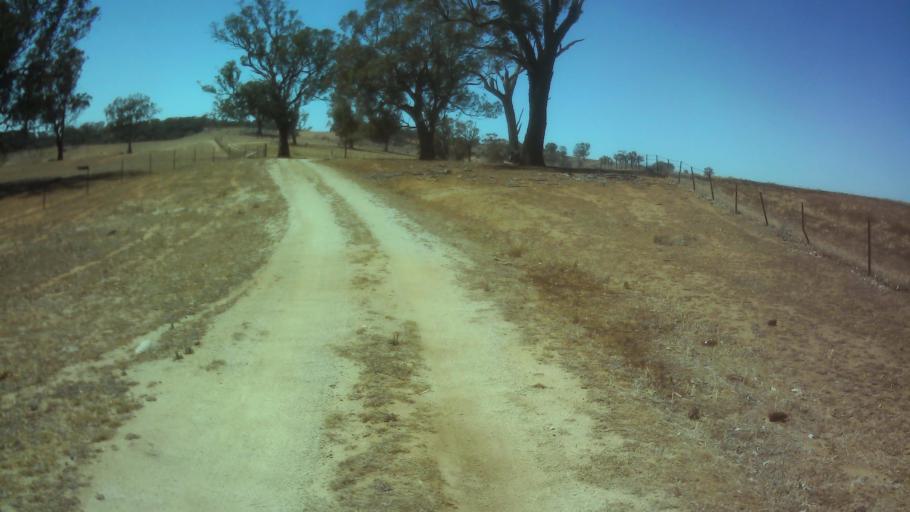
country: AU
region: New South Wales
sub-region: Cowra
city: Cowra
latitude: -33.8898
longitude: 148.4989
